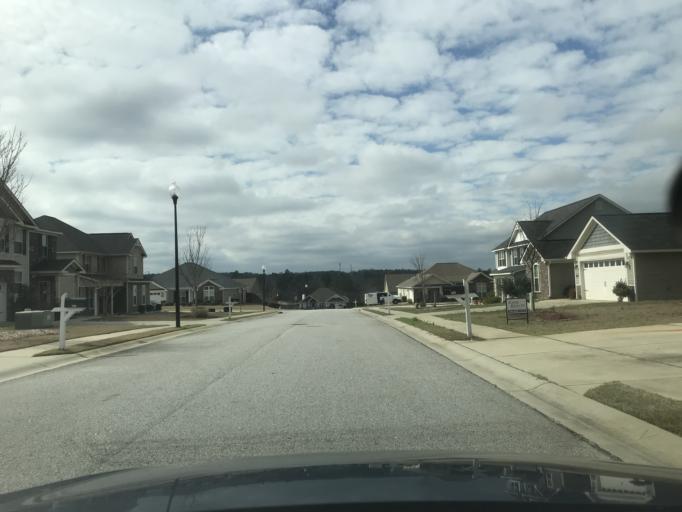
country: US
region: Georgia
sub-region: Columbia County
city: Grovetown
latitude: 33.4405
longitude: -82.1485
